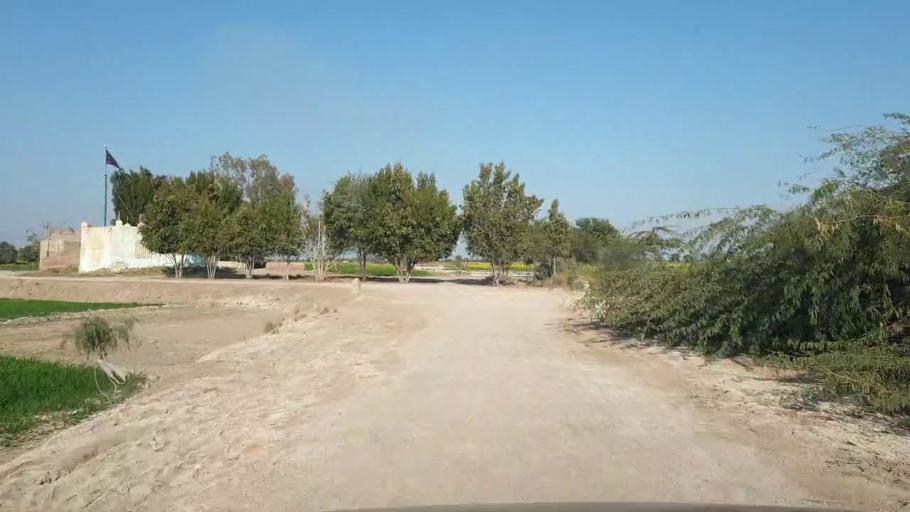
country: PK
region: Sindh
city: Shahpur Chakar
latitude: 26.1667
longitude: 68.6648
